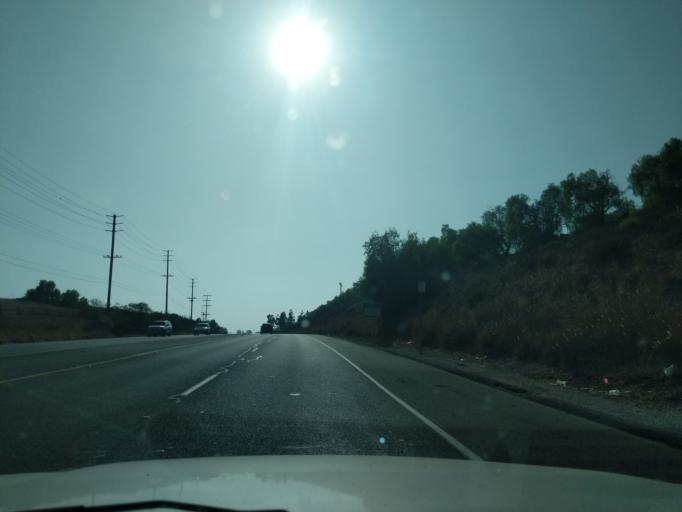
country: US
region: California
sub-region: Ventura County
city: Simi Valley
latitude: 34.2739
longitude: -118.8153
